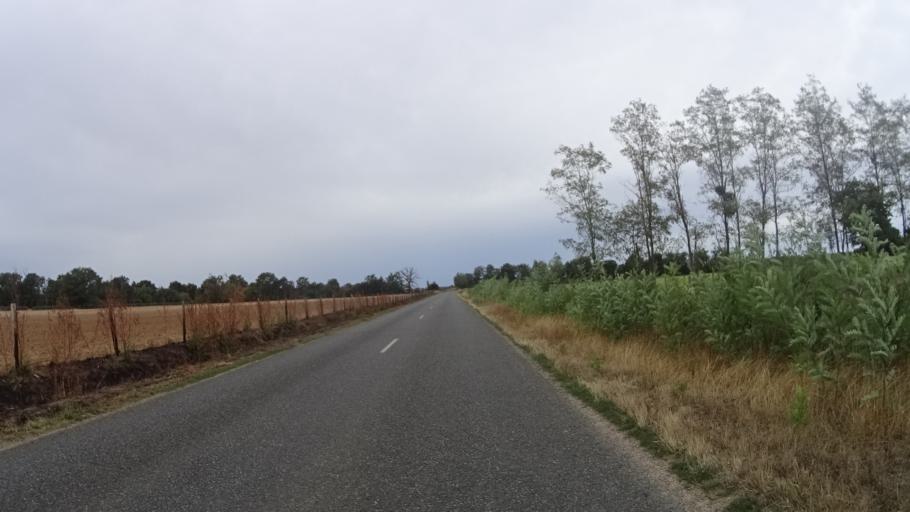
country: FR
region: Bourgogne
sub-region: Departement de la Nievre
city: Lucenay-les-Aix
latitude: 46.7708
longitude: 3.5525
